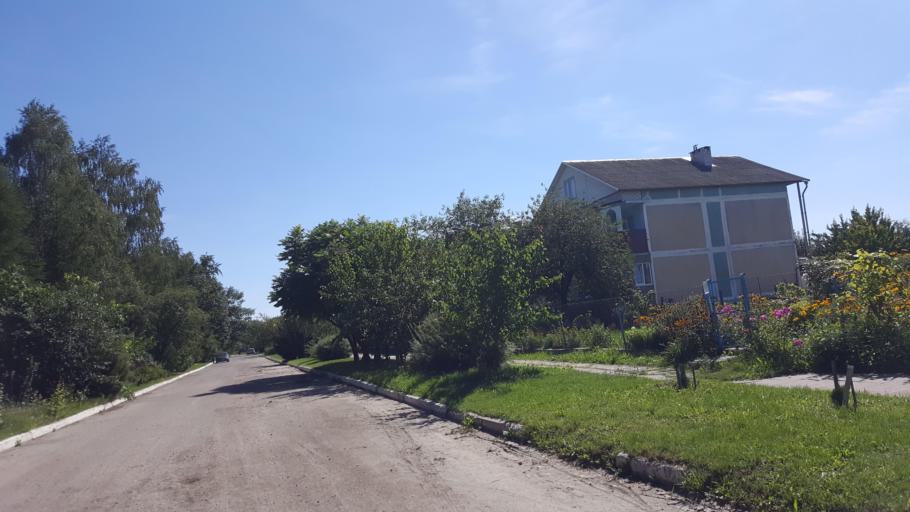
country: BY
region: Brest
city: Charnawchytsy
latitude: 52.2679
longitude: 23.5958
